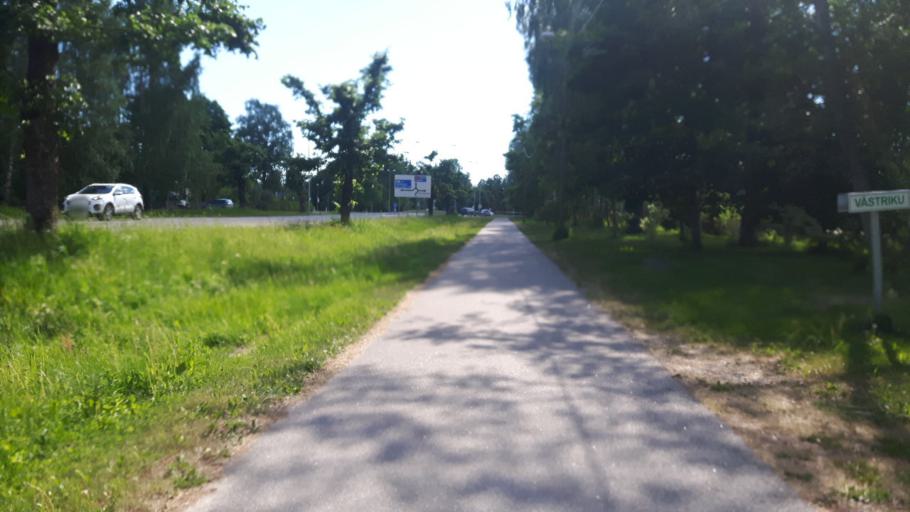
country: EE
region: Paernumaa
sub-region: Paikuse vald
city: Paikuse
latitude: 58.3770
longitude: 24.6247
